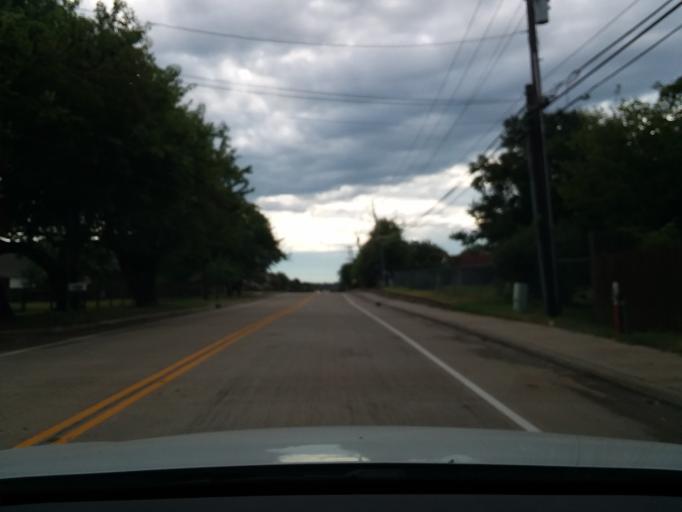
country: US
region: Texas
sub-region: Denton County
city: Highland Village
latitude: 33.0606
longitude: -97.0573
